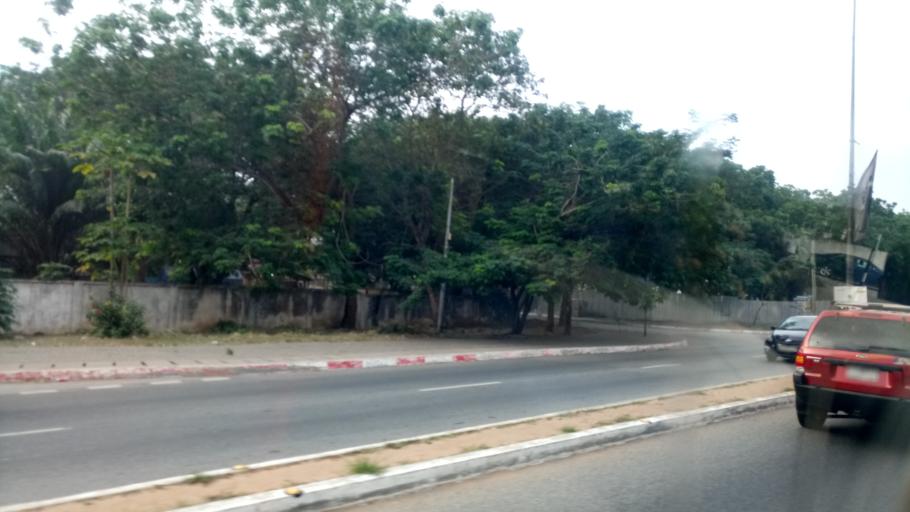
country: GH
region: Greater Accra
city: Accra
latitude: 5.5620
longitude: -0.1959
